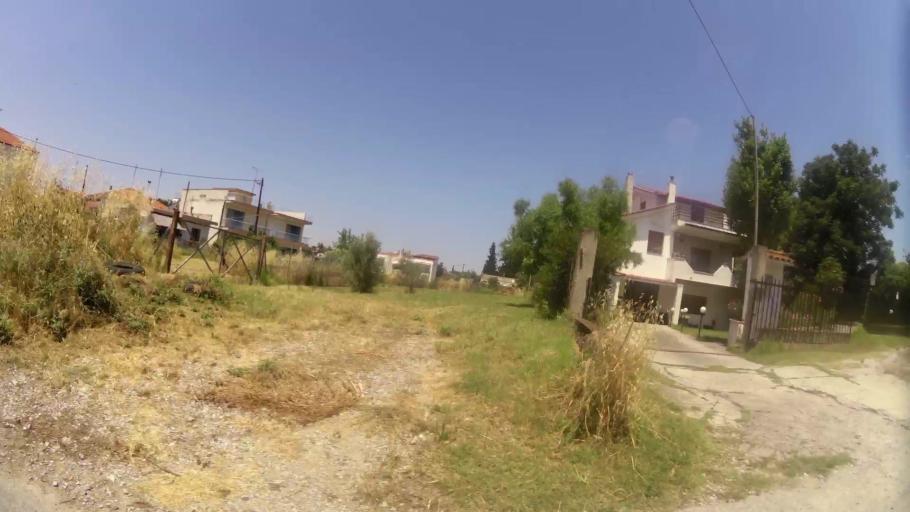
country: GR
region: Central Macedonia
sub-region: Nomos Thessalonikis
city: Epanomi
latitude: 40.4314
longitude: 22.9315
